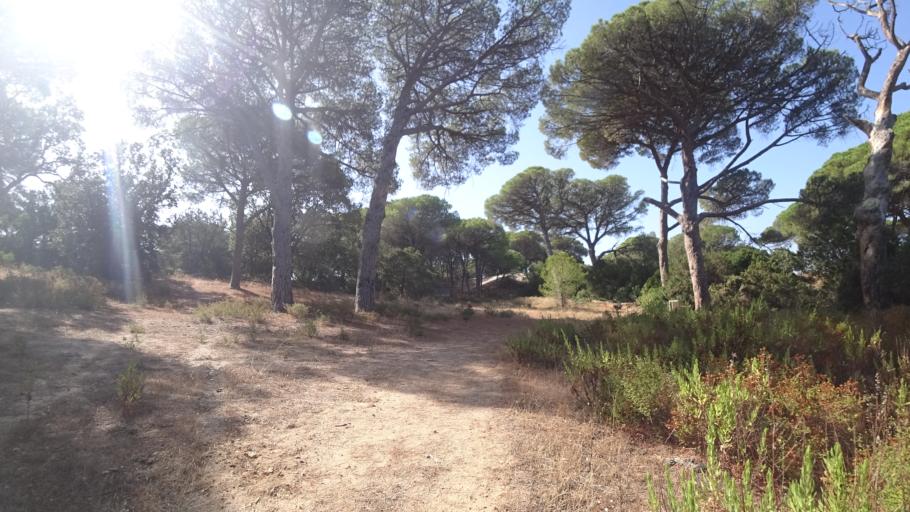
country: FR
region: Corsica
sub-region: Departement de la Corse-du-Sud
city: Porto-Vecchio
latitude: 41.5603
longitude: 9.3371
